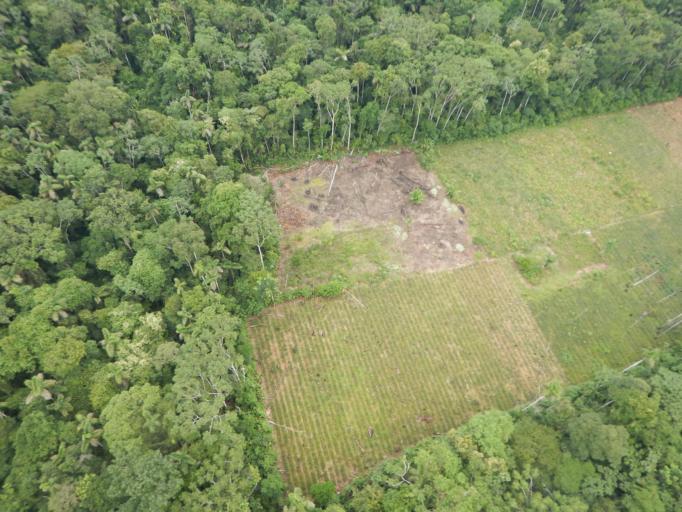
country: BO
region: Cochabamba
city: Chimore
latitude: -17.1855
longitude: -64.7512
